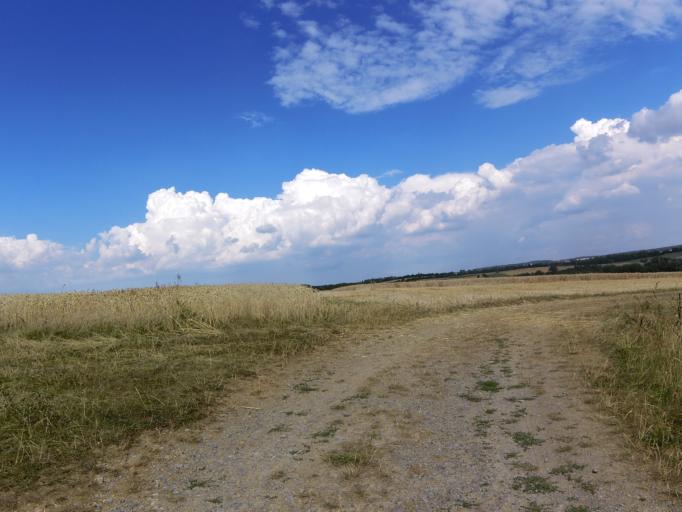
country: DE
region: Bavaria
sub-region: Regierungsbezirk Unterfranken
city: Rimpar
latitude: 49.8274
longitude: 9.9670
